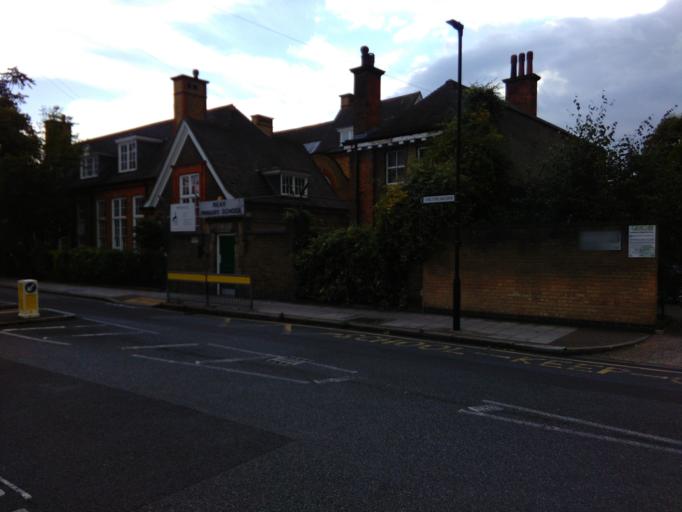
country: GB
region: England
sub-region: Greater London
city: Kennington
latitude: 51.4777
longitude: -0.1146
